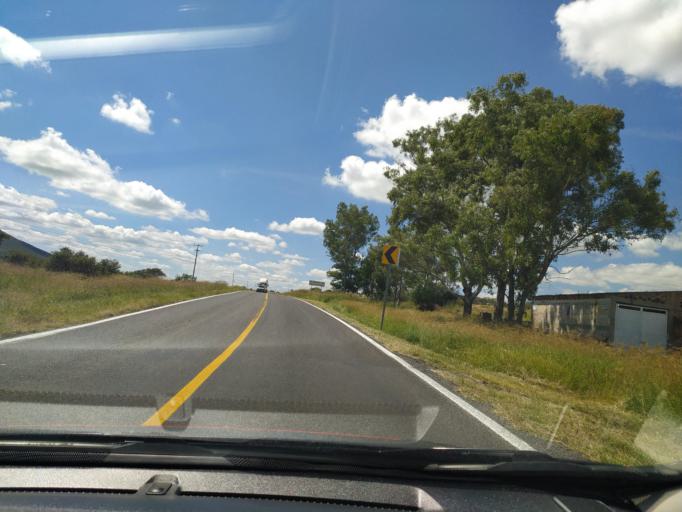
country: MX
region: Jalisco
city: San Miguel el Alto
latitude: 21.0250
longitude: -102.4298
